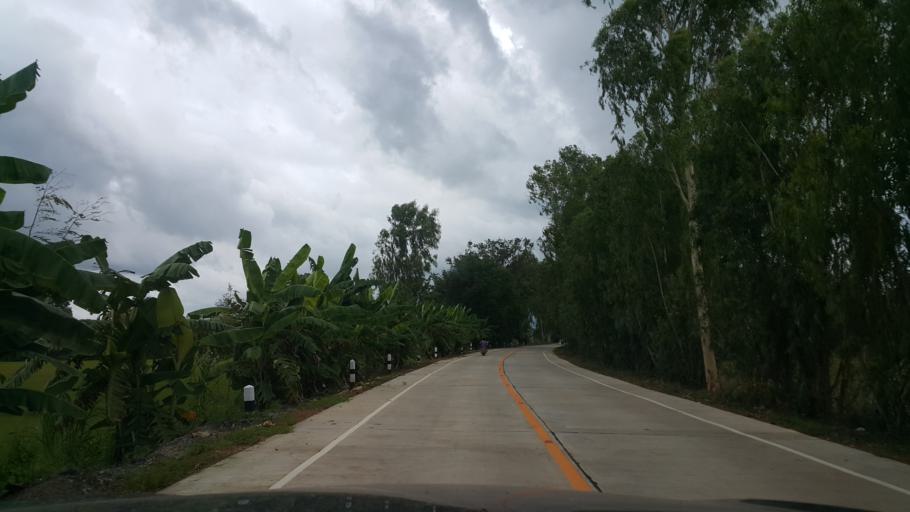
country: TH
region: Sukhothai
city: Kong Krailat
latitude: 16.9255
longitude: 99.8965
